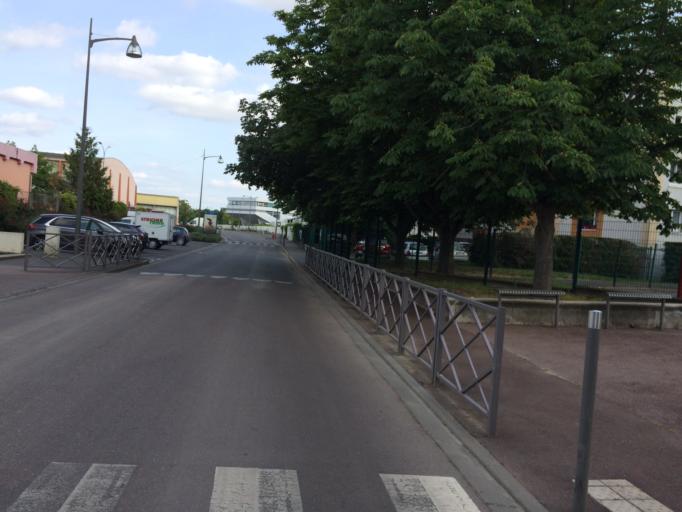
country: FR
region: Ile-de-France
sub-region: Departement de l'Essonne
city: Longjumeau
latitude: 48.6928
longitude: 2.2997
